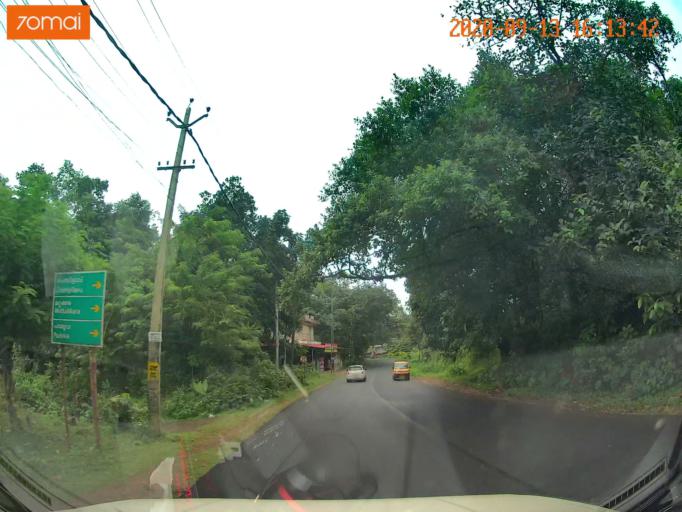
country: IN
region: Kerala
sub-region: Kottayam
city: Palackattumala
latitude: 9.6891
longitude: 76.6287
